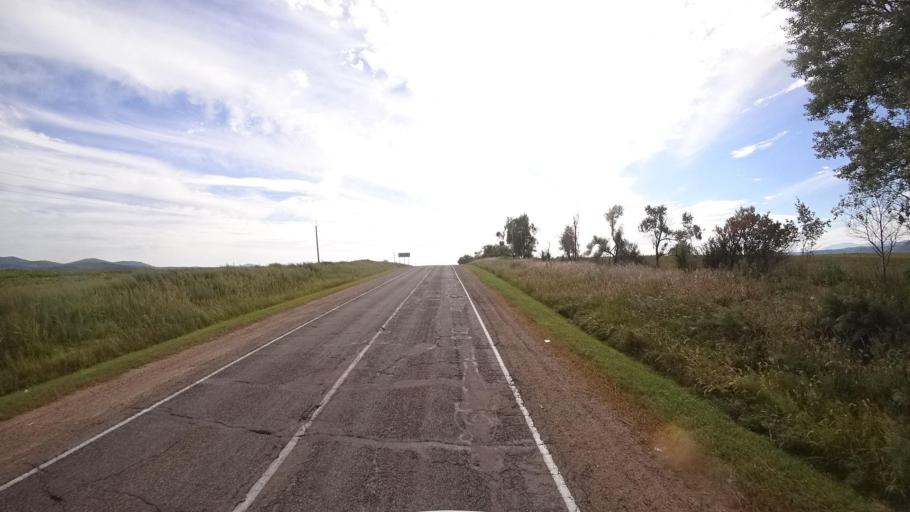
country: RU
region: Primorskiy
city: Dostoyevka
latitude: 44.3161
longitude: 133.4647
